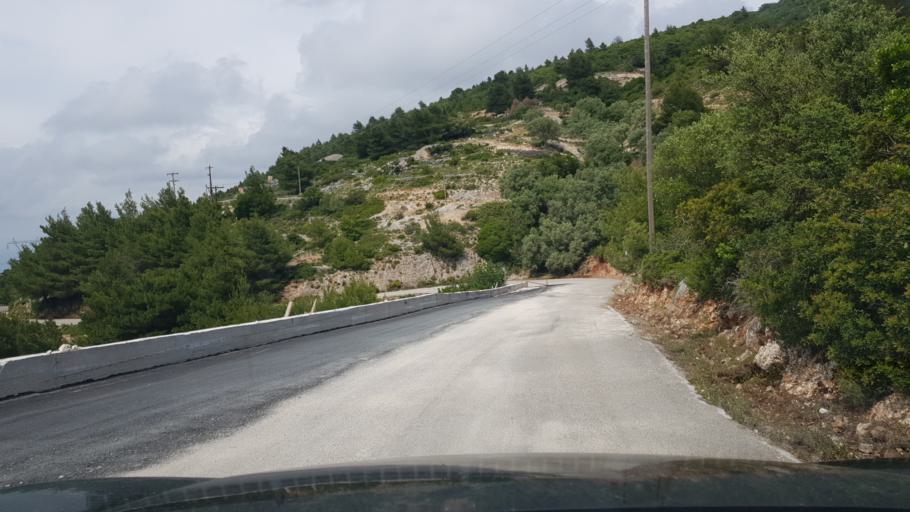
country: GR
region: Ionian Islands
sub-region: Lefkada
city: Nidri
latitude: 38.6199
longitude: 20.5645
